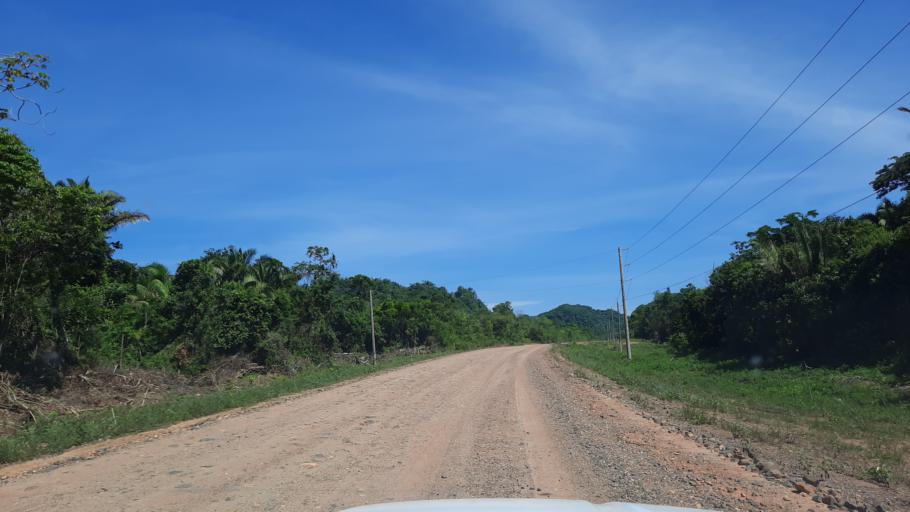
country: BZ
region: Stann Creek
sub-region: Dangriga
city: Dangriga
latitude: 17.1668
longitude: -88.3646
